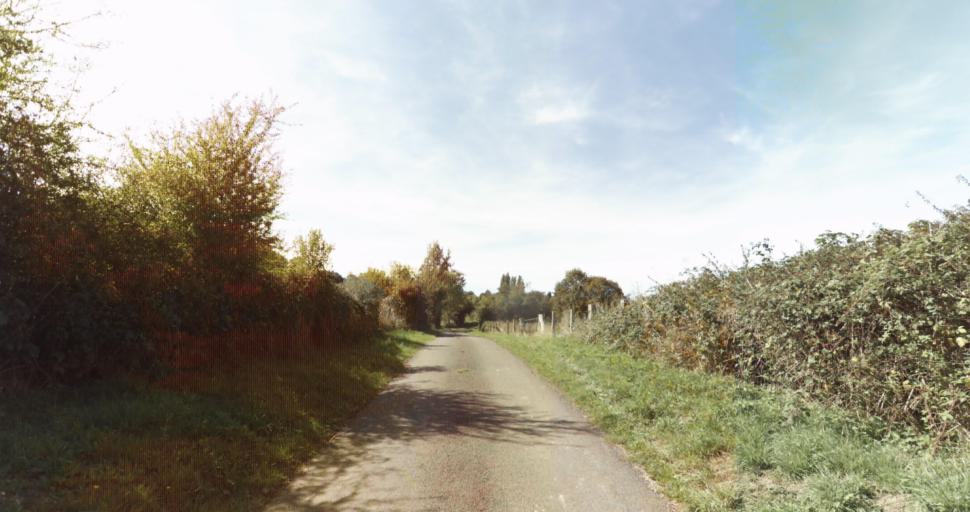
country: FR
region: Lower Normandy
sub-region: Departement de l'Orne
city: Gace
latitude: 48.7330
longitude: 0.2366
